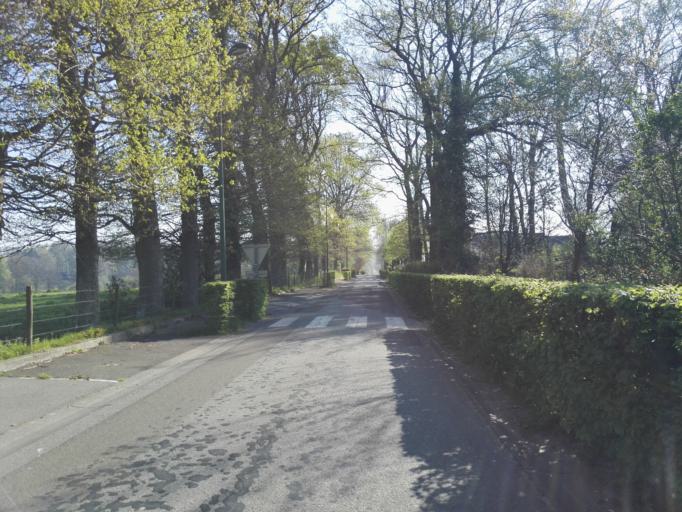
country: FR
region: Haute-Normandie
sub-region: Departement de la Seine-Maritime
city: Grainville-la-Teinturiere
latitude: 49.7386
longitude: 0.7110
